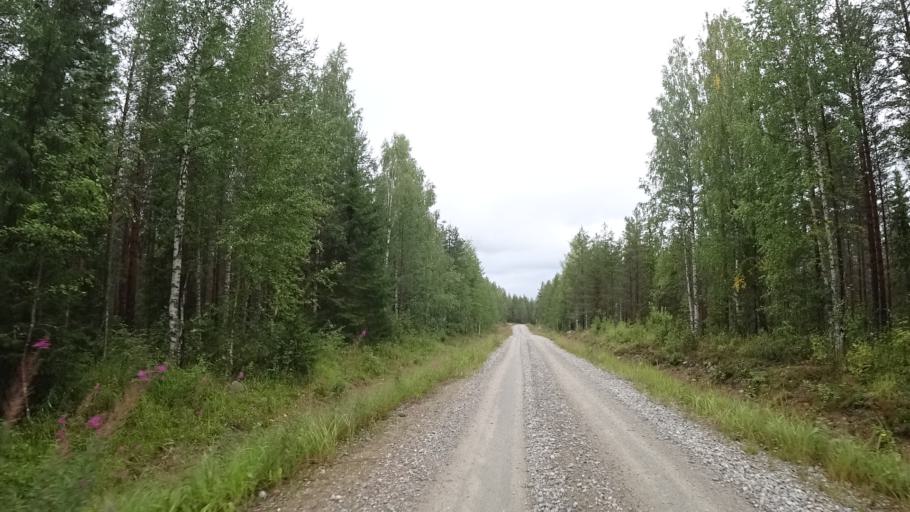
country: FI
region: North Karelia
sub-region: Pielisen Karjala
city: Lieksa
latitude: 63.4760
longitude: 30.2618
